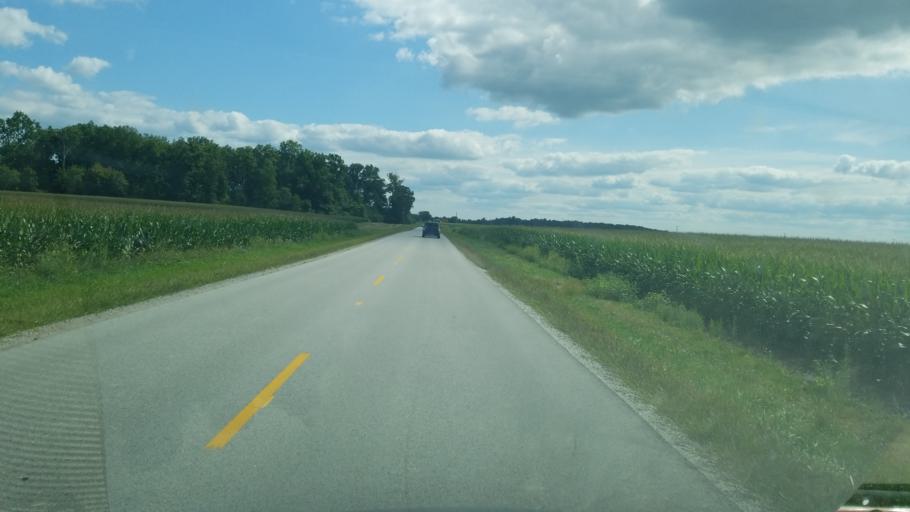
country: US
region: Ohio
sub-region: Logan County
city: Lakeview
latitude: 40.5623
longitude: -83.9756
